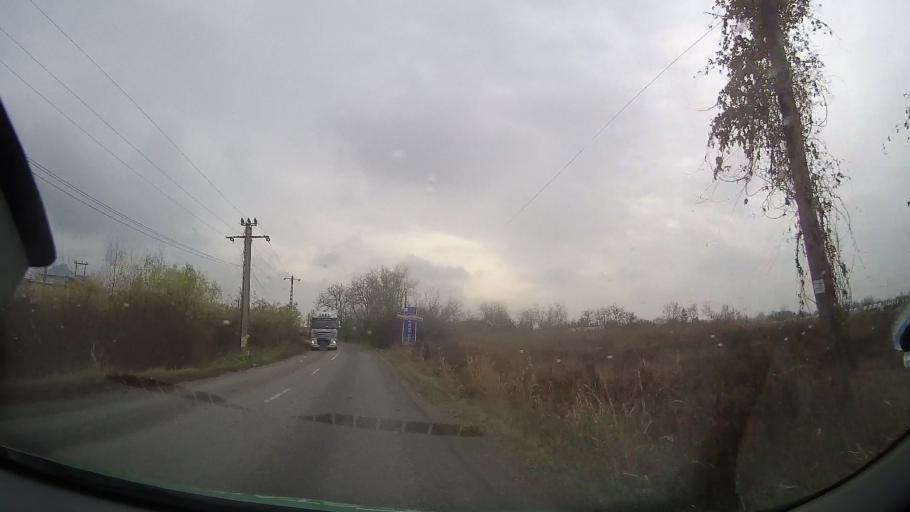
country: RO
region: Prahova
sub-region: Comuna Gherghita
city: Gherghita
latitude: 44.8019
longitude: 26.2668
